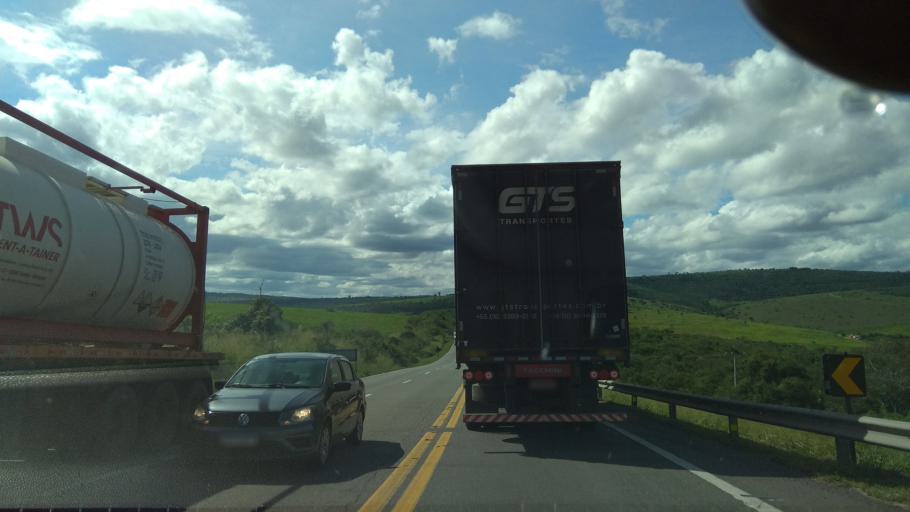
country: BR
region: Bahia
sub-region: Santa Ines
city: Santa Ines
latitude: -13.1732
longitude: -39.9992
